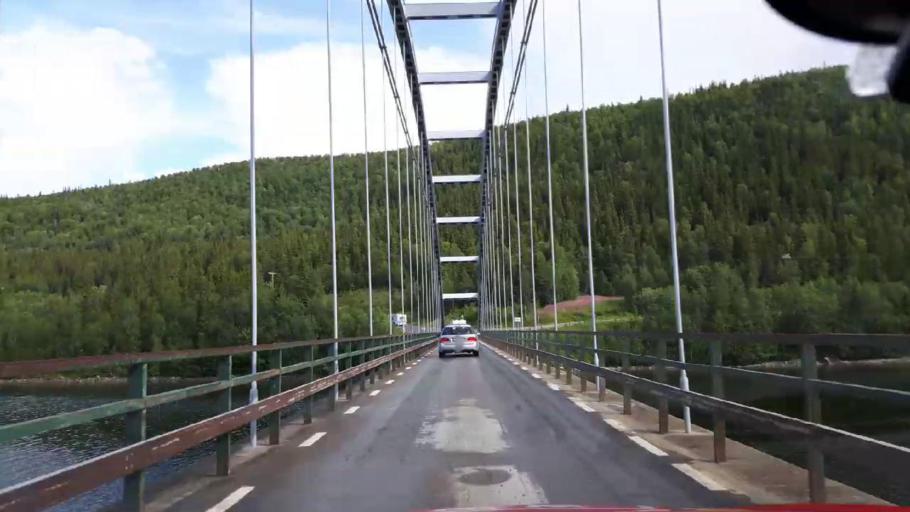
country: SE
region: Vaesterbotten
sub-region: Vilhelmina Kommun
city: Sjoberg
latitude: 65.0315
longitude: 15.1392
